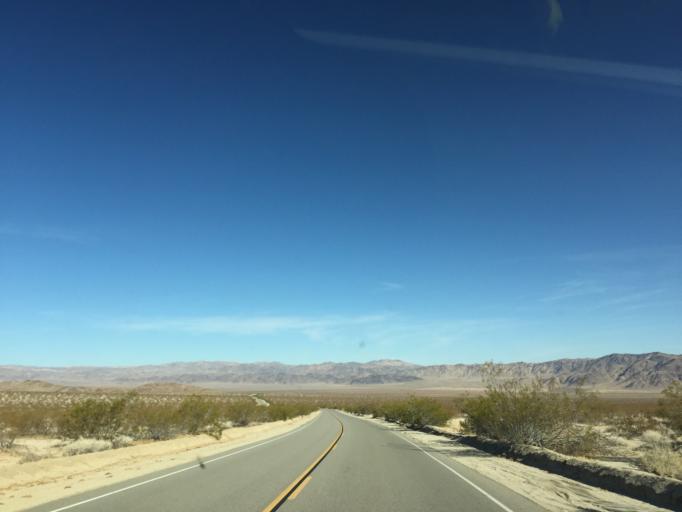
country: US
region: California
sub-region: San Bernardino County
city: Twentynine Palms
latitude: 33.8675
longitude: -115.7991
